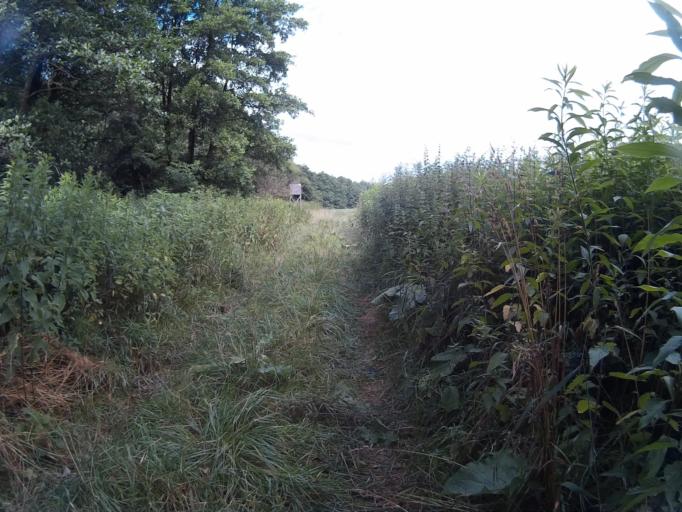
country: HU
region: Veszprem
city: Urkut
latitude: 47.1327
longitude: 17.6711
